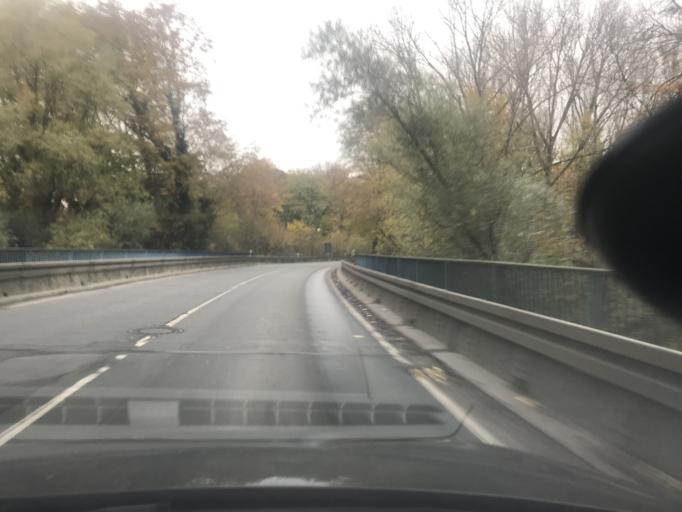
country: DE
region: North Rhine-Westphalia
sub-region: Regierungsbezirk Arnsberg
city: Welver
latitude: 51.6954
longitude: 7.9499
